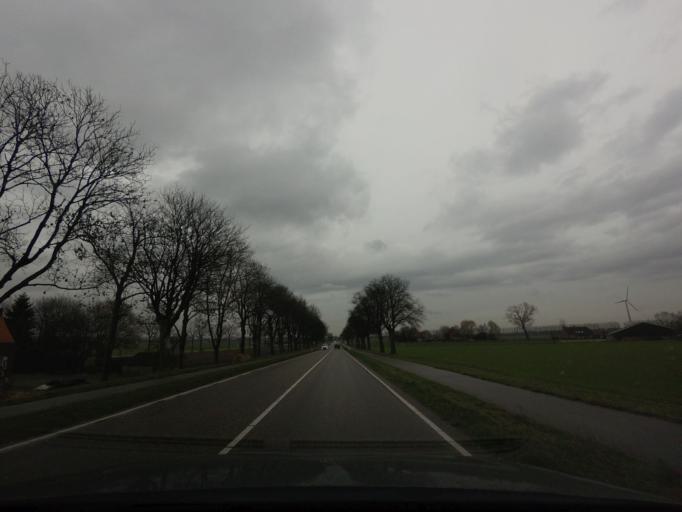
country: NL
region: North Brabant
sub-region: Gemeente Moerdijk
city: Klundert
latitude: 51.6233
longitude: 4.6360
